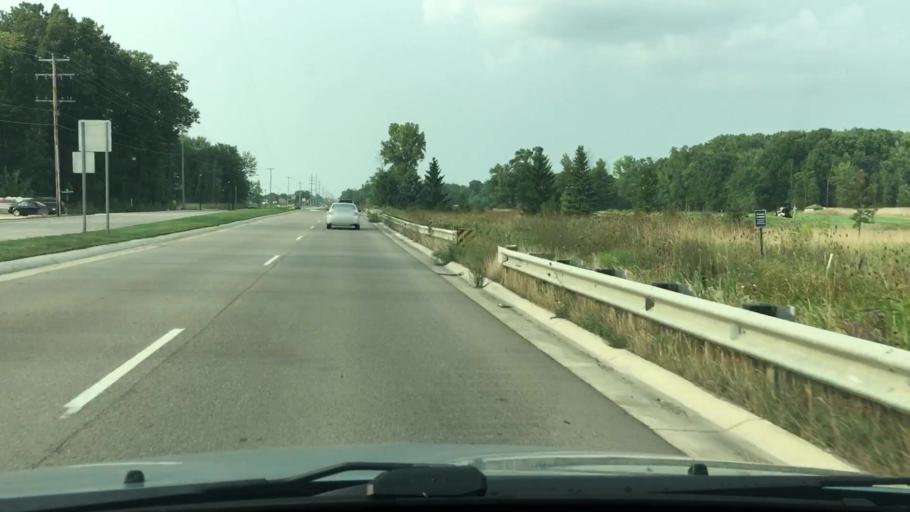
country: US
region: Michigan
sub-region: Ottawa County
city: Allendale
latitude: 42.9661
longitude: -85.9041
